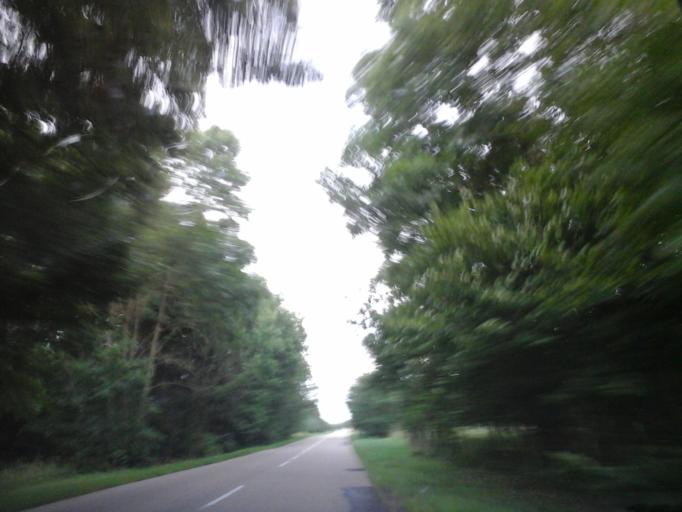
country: PL
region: West Pomeranian Voivodeship
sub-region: Powiat goleniowski
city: Nowogard
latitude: 53.6946
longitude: 15.0641
